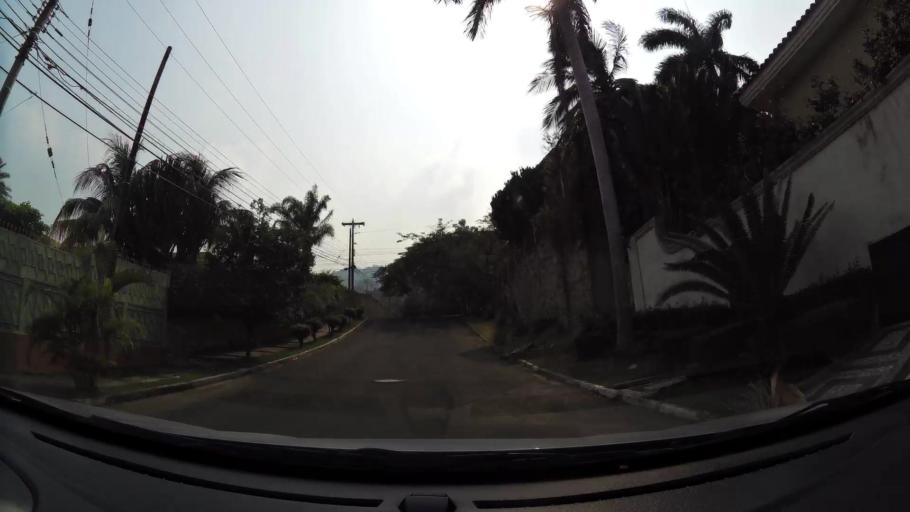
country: HN
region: Cortes
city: Armenta
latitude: 15.4958
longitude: -88.0471
